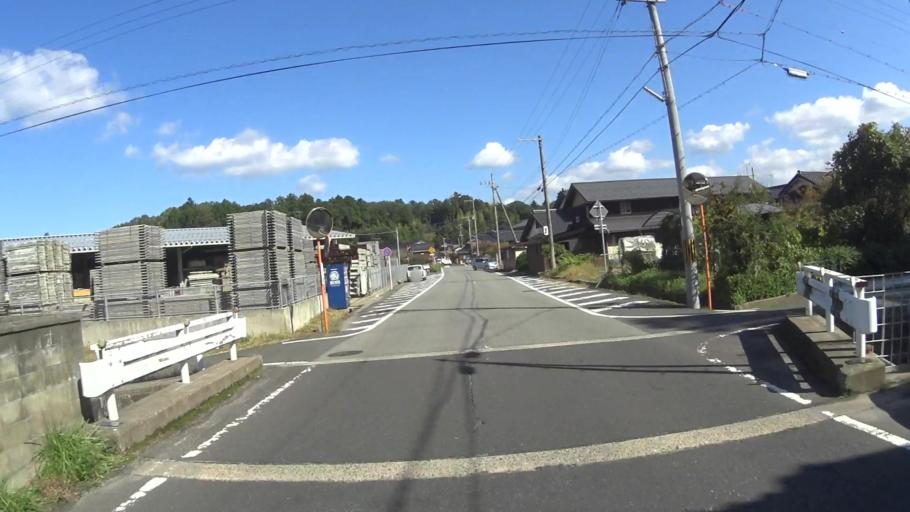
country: JP
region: Kyoto
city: Miyazu
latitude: 35.6308
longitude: 135.0713
